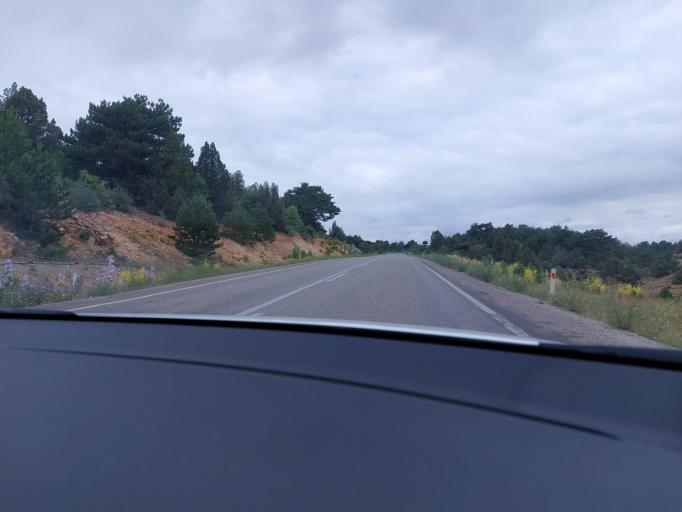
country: TR
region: Konya
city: Doganbey
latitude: 37.8912
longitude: 31.8204
